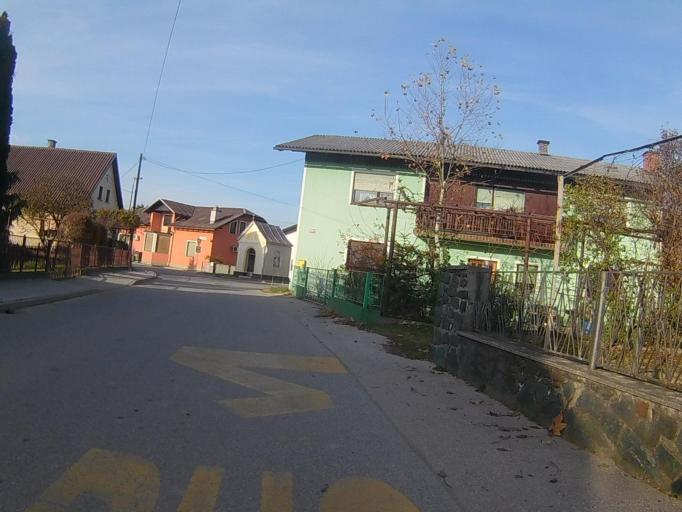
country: SI
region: Duplek
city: Zgornji Duplek
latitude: 46.5234
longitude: 15.7052
